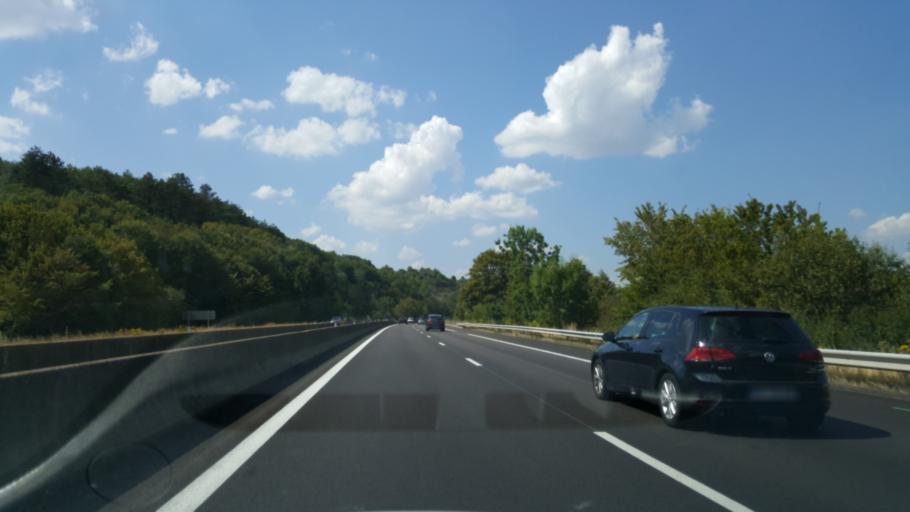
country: FR
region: Bourgogne
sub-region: Departement de la Cote-d'Or
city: Pouilly-en-Auxois
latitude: 47.1764
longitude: 4.6864
